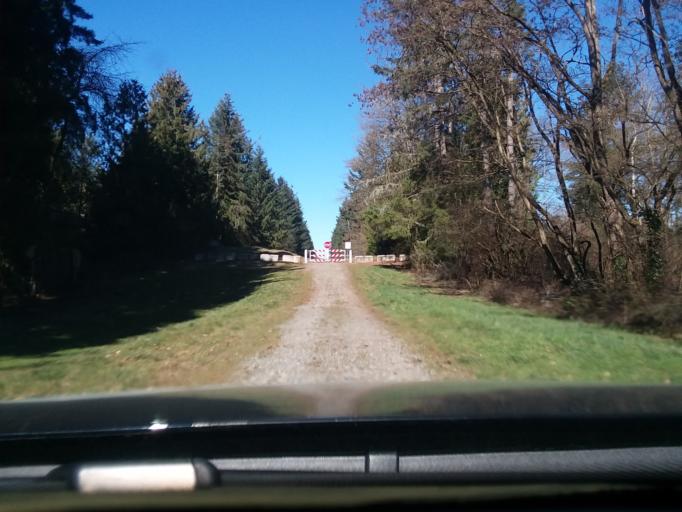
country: US
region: Washington
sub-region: Pierce County
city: Summit
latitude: 47.1664
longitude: -122.3422
